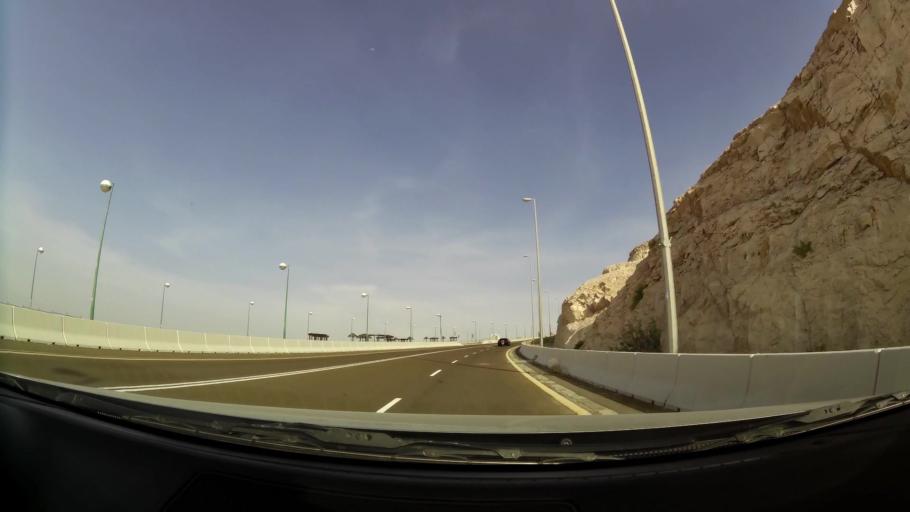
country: AE
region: Abu Dhabi
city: Al Ain
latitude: 24.0825
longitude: 55.7686
